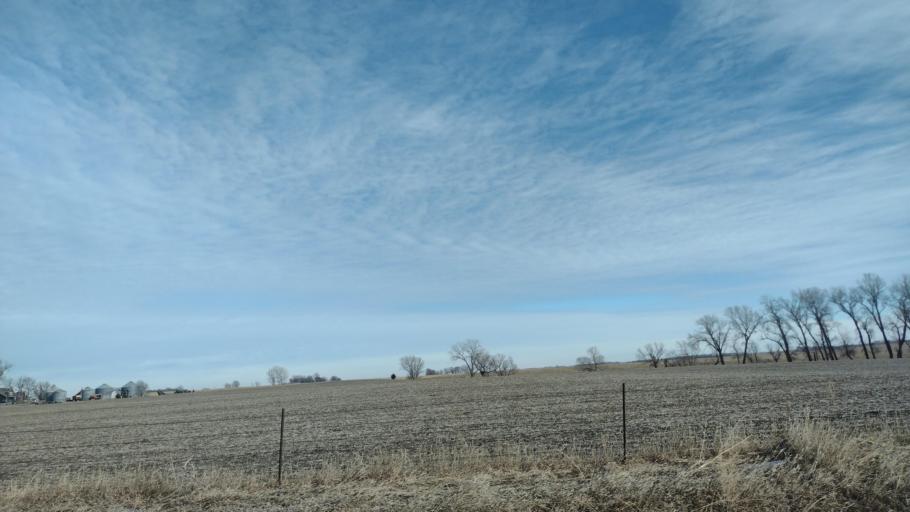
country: US
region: South Dakota
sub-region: Union County
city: Beresford
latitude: 42.9479
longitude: -96.8055
